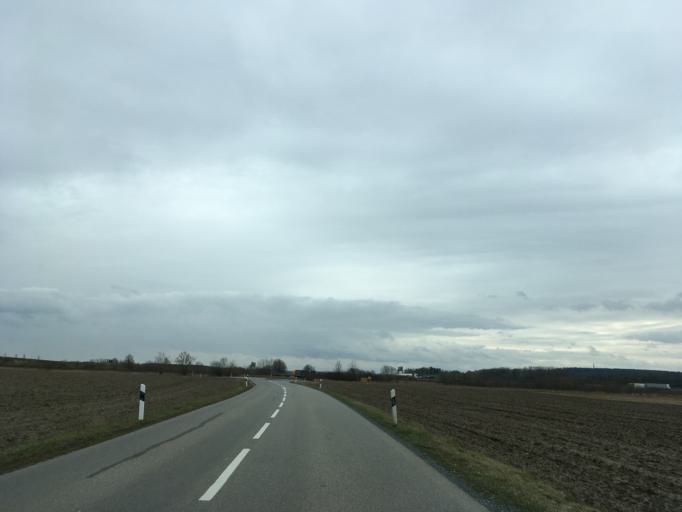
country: DE
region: Bavaria
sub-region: Upper Bavaria
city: Ampfing
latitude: 48.2543
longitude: 12.3885
